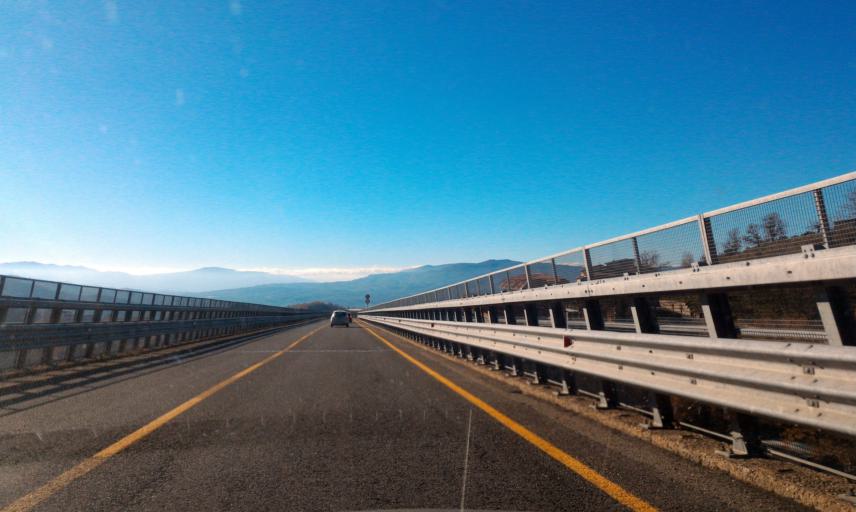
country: IT
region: Calabria
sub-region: Provincia di Cosenza
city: Spezzano Piccolo
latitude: 39.2915
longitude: 16.3496
